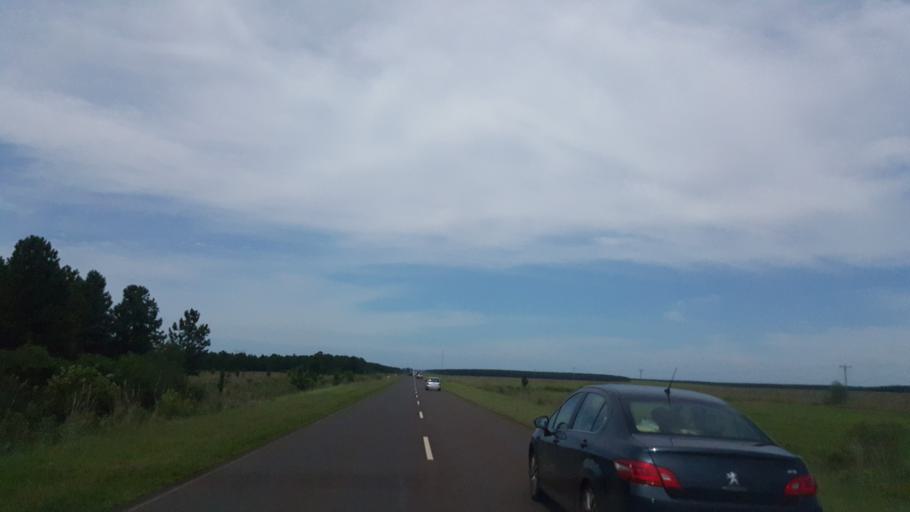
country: PY
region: Itapua
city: San Juan del Parana
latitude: -27.5092
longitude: -56.1326
